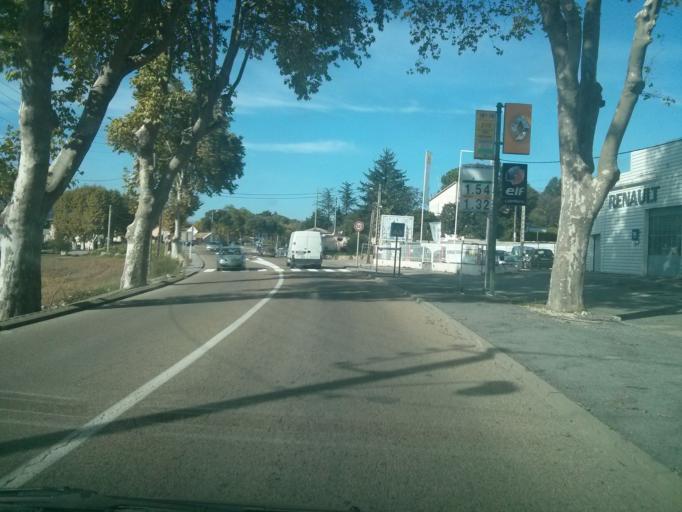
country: FR
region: Languedoc-Roussillon
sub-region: Departement du Gard
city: Quissac
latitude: 43.9068
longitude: 4.0048
